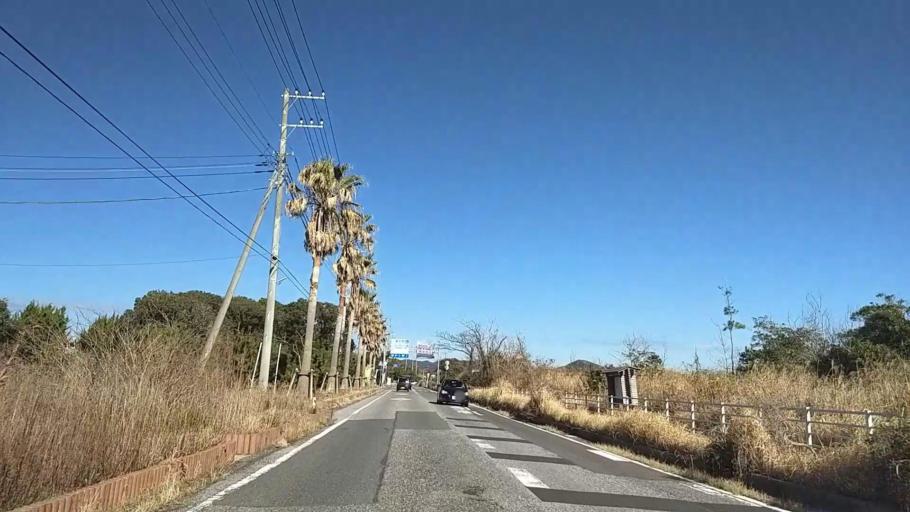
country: JP
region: Chiba
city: Tateyama
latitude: 35.0074
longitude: 139.9765
